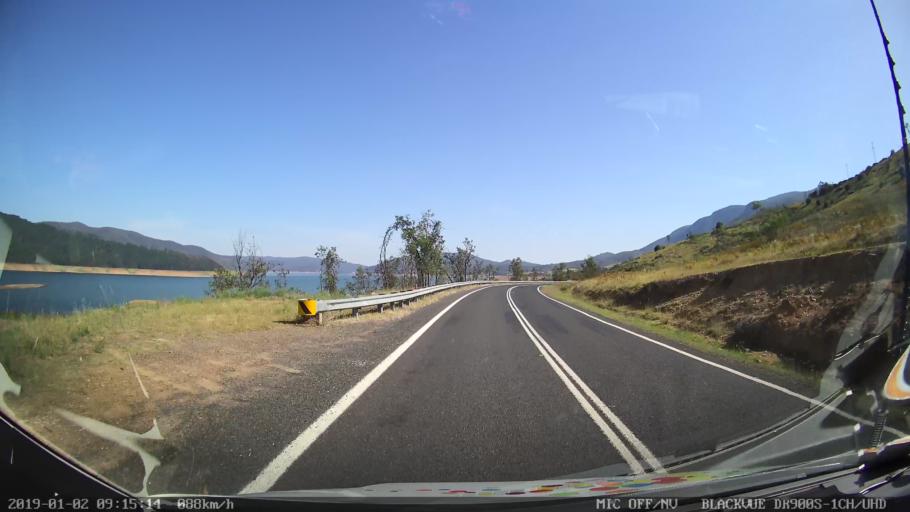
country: AU
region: New South Wales
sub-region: Tumut Shire
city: Tumut
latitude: -35.4675
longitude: 148.2785
